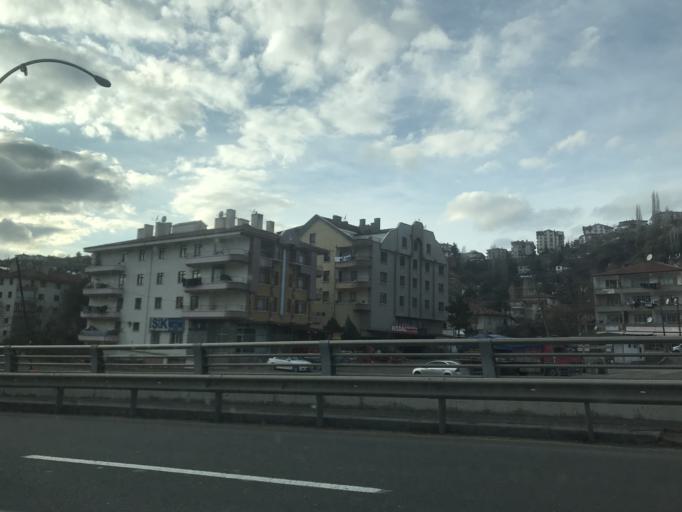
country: TR
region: Ankara
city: Mamak
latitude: 39.9893
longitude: 32.8984
